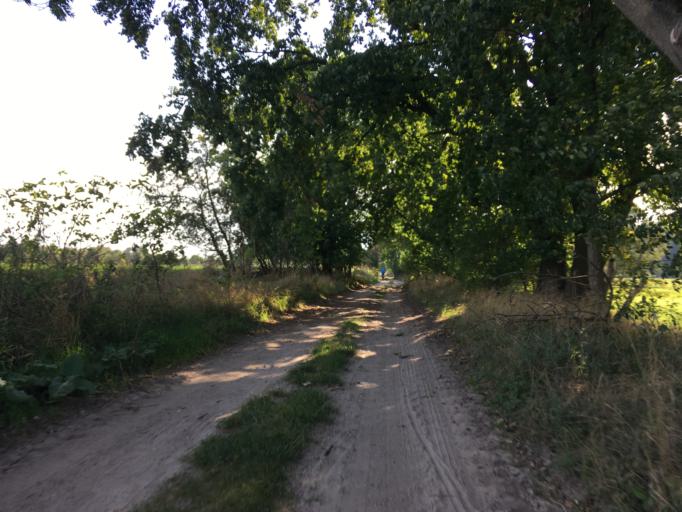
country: DE
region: Brandenburg
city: Altlandsberg
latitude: 52.5475
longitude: 13.7247
